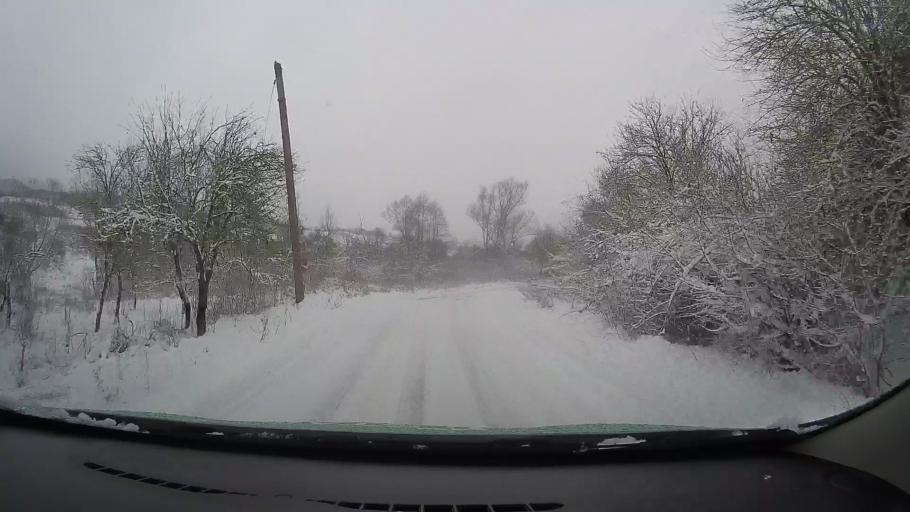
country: RO
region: Hunedoara
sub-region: Comuna Carjiti
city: Carjiti
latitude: 45.8352
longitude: 22.8395
